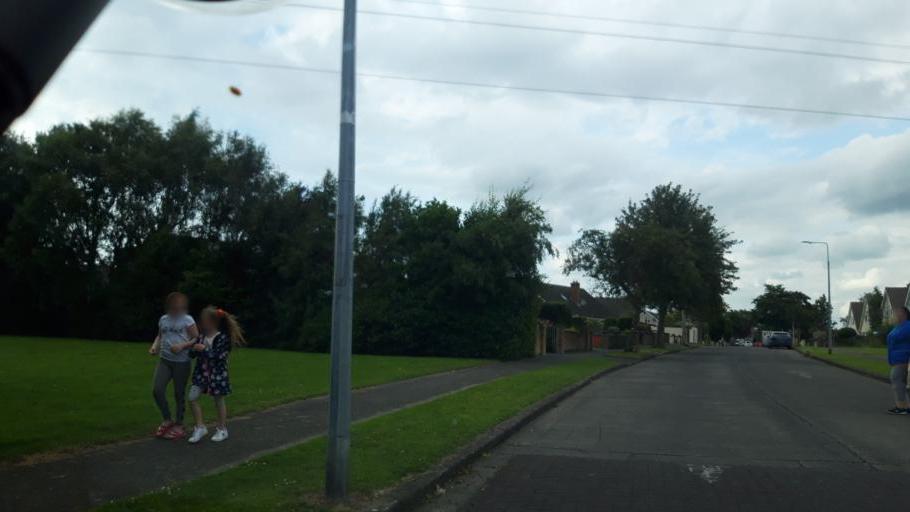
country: IE
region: Leinster
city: Hartstown
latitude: 53.3927
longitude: -6.4236
